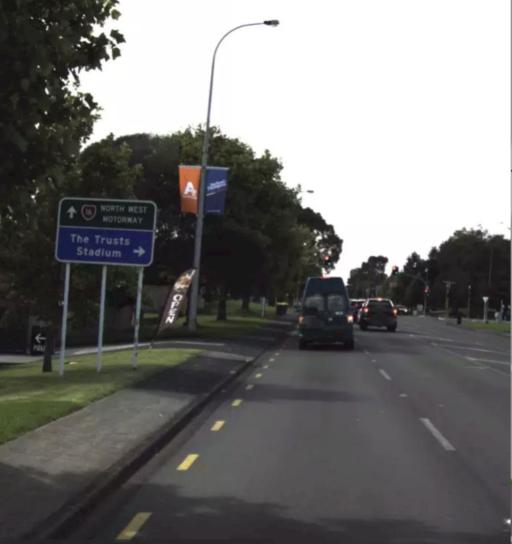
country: NZ
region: Auckland
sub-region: Auckland
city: Rosebank
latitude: -36.8633
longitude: 174.6293
